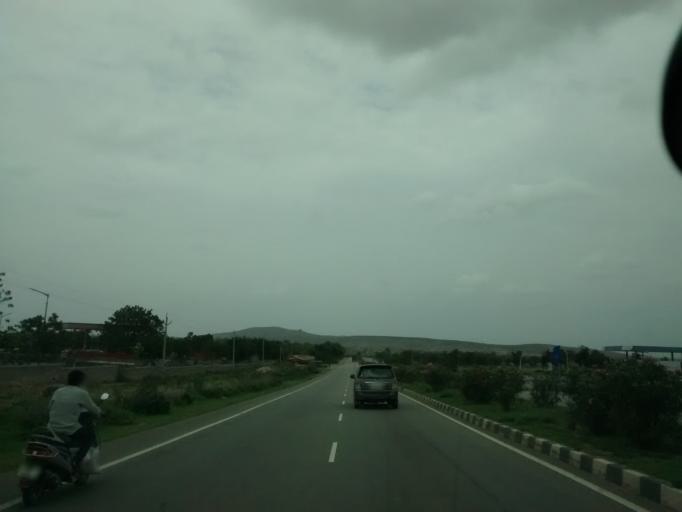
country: IN
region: Andhra Pradesh
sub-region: Kurnool
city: Ramapuram
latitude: 15.2547
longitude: 77.7535
